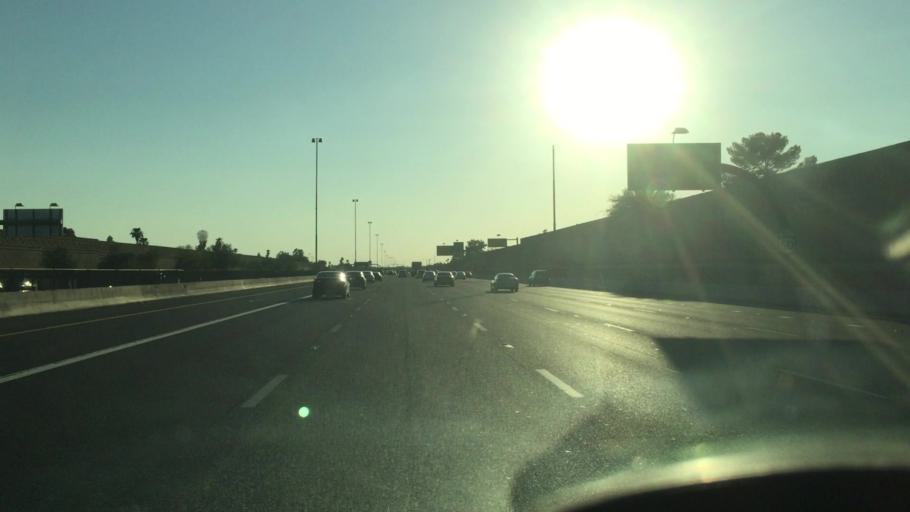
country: US
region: Arizona
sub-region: Maricopa County
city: Tempe
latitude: 33.3864
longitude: -111.9177
